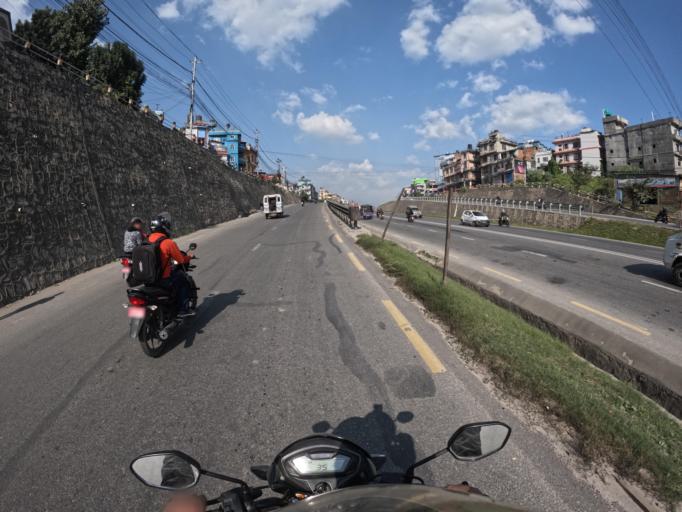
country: NP
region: Central Region
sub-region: Bagmati Zone
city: Patan
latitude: 27.6745
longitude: 85.3430
